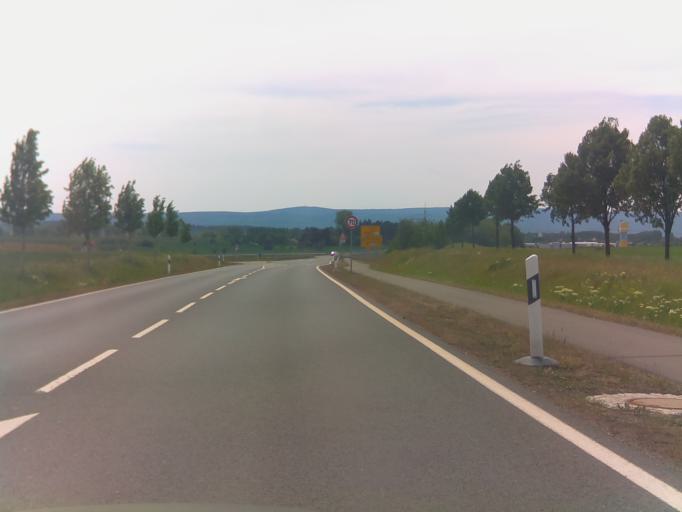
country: DE
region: Saxony-Anhalt
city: Ditfurt
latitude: 51.8099
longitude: 11.1996
